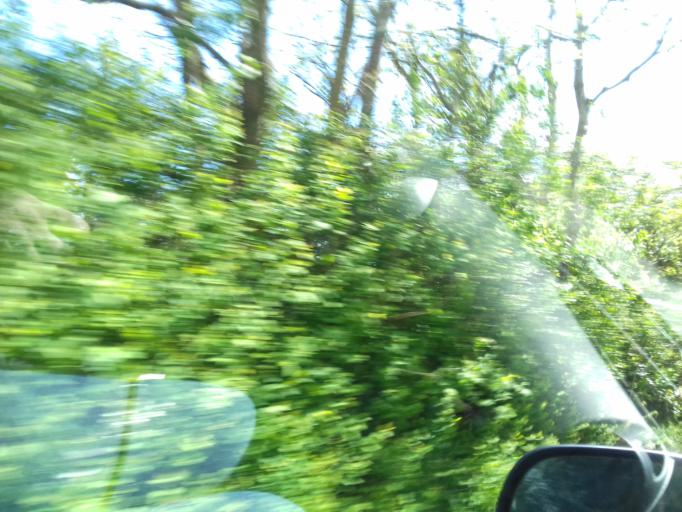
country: IE
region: Munster
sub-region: Waterford
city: Dunmore East
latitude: 52.2450
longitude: -6.8610
